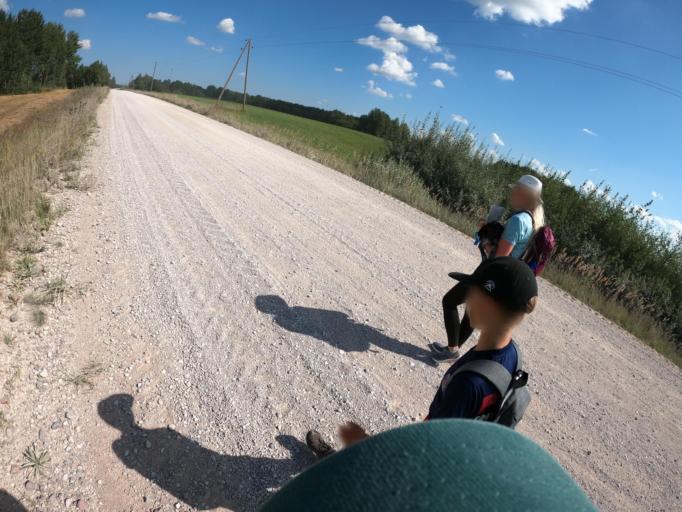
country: LT
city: Skuodas
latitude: 56.3586
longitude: 21.5459
